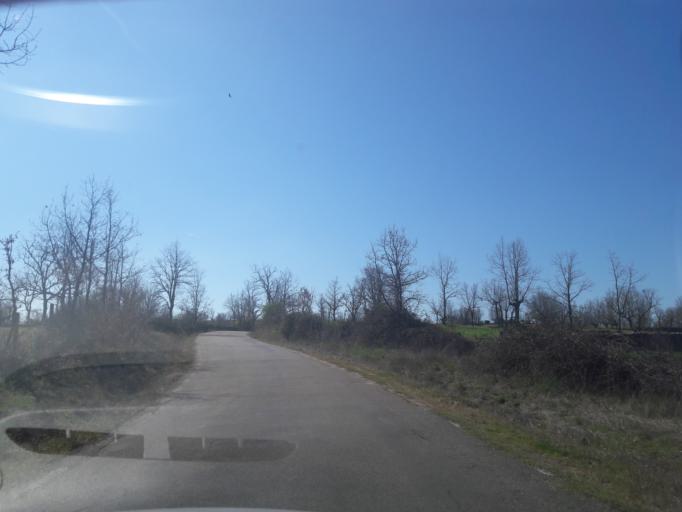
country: ES
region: Castille and Leon
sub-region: Provincia de Salamanca
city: Valsalabroso
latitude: 41.1445
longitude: -6.4860
